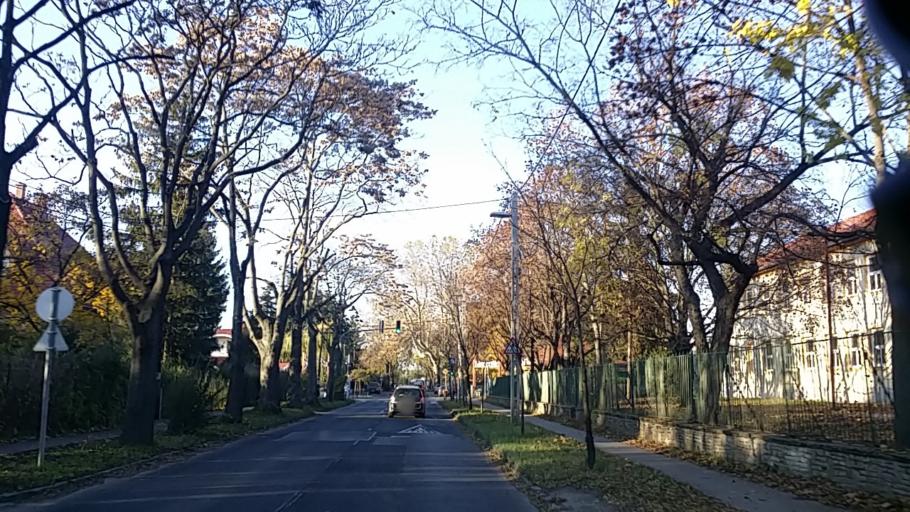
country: HU
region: Budapest
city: Budapest XVI. keruelet
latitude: 47.5123
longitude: 19.2041
